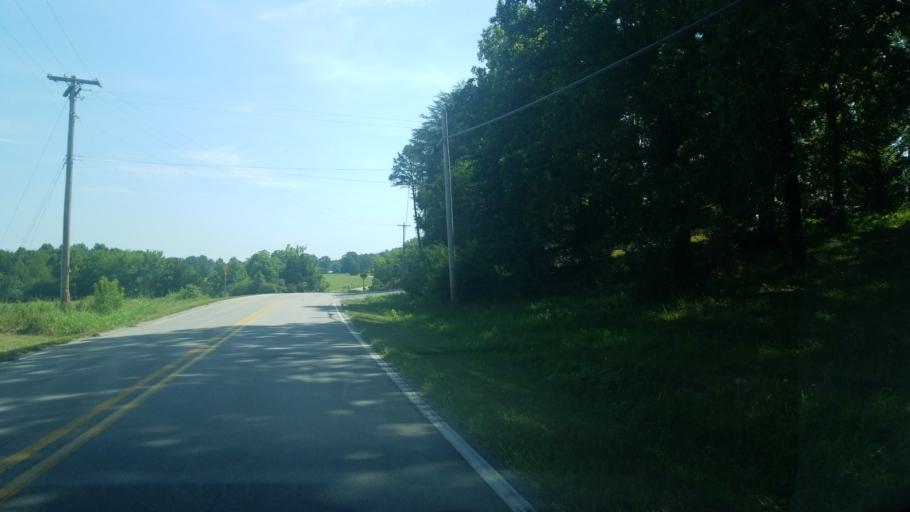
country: US
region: Tennessee
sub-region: Hamilton County
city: Sale Creek
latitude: 35.3145
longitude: -85.0283
